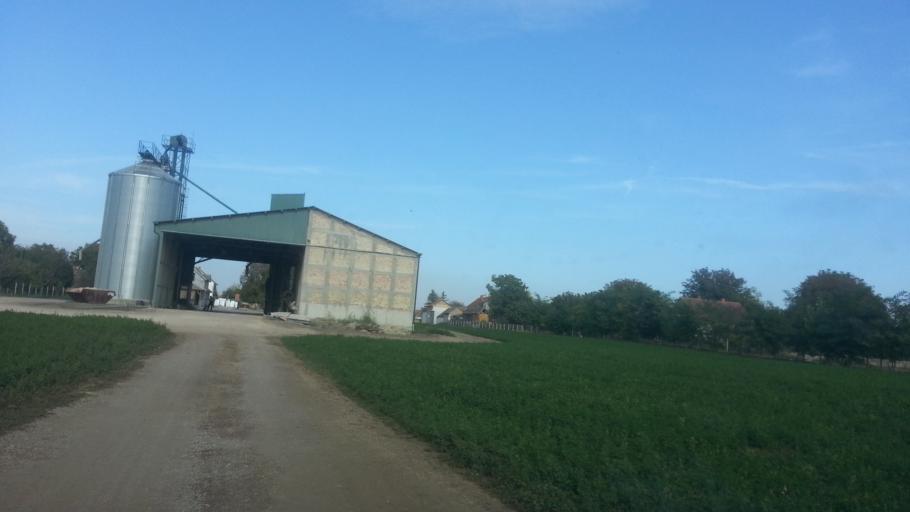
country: RS
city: Belegis
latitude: 45.0185
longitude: 20.3149
